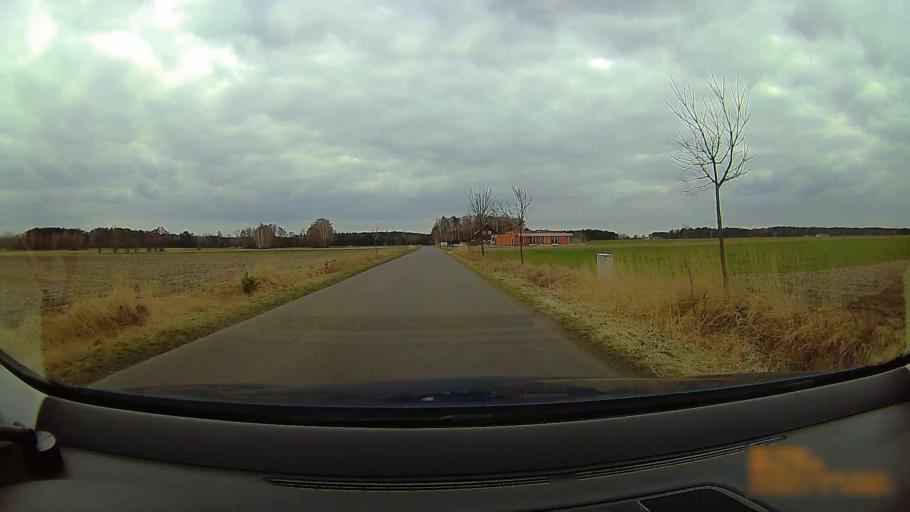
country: PL
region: Greater Poland Voivodeship
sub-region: Powiat koninski
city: Rychwal
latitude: 52.0891
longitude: 18.1406
